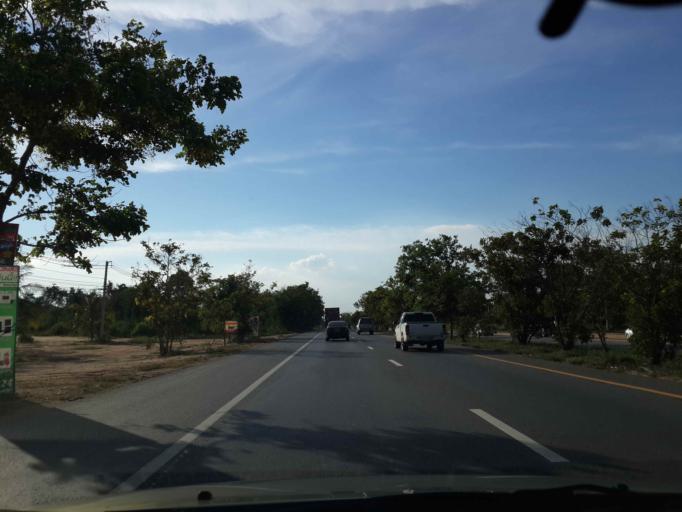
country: TH
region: Chon Buri
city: Phatthaya
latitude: 12.9407
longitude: 100.9951
